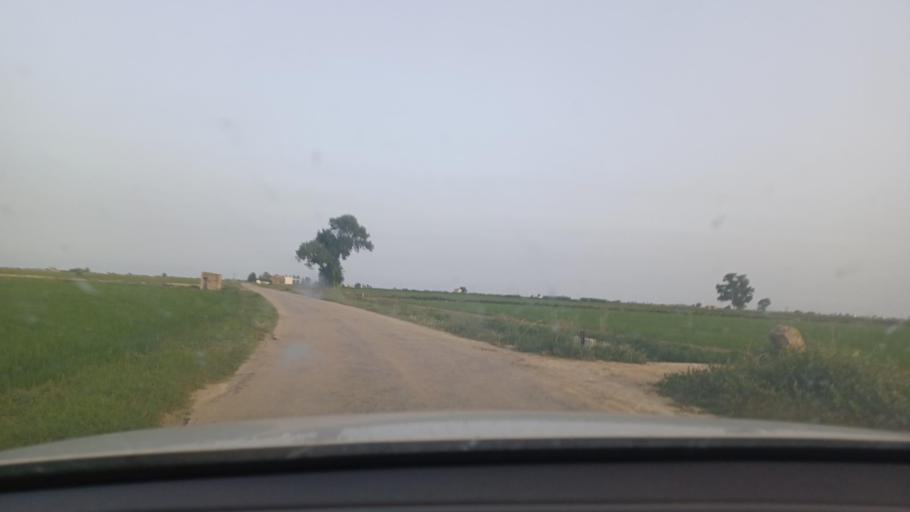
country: ES
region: Catalonia
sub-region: Provincia de Tarragona
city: Deltebre
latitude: 40.6882
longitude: 0.6522
